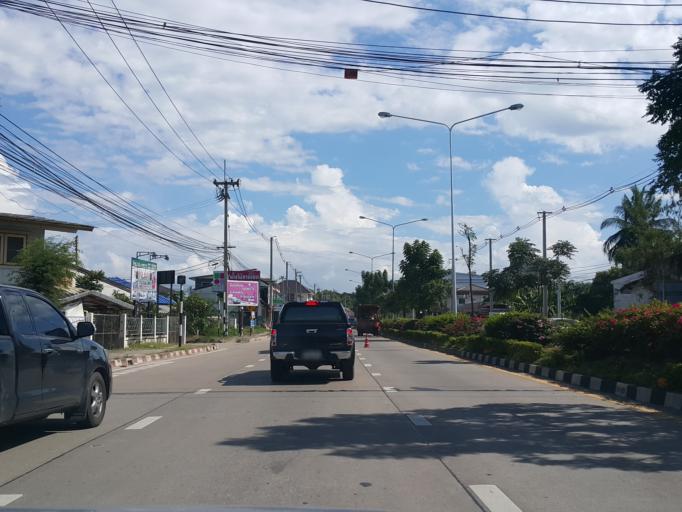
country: TH
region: Chiang Mai
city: San Sai
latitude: 18.8071
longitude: 99.0284
